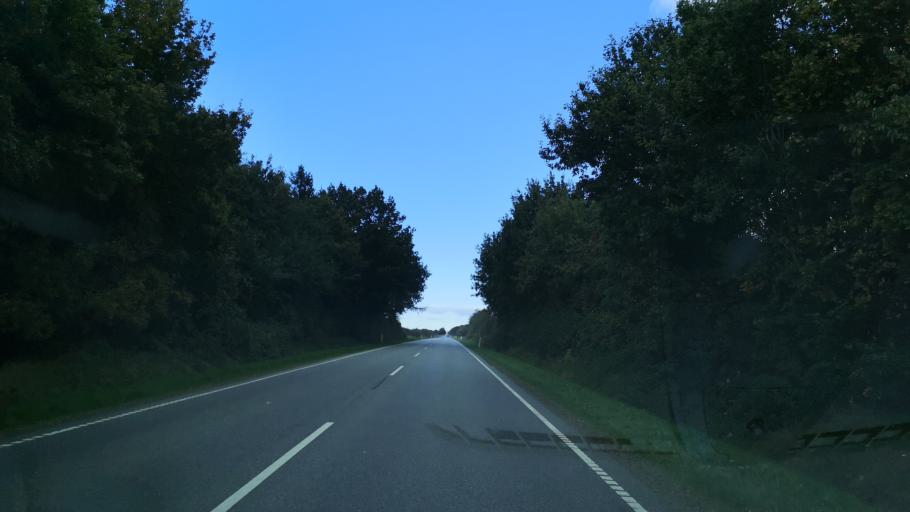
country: DK
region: South Denmark
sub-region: Tonder Kommune
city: Sherrebek
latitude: 55.0969
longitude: 8.8176
